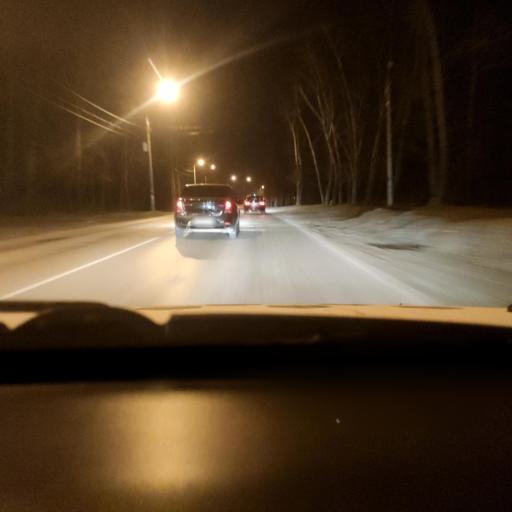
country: RU
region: Perm
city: Perm
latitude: 58.1193
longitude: 56.3687
